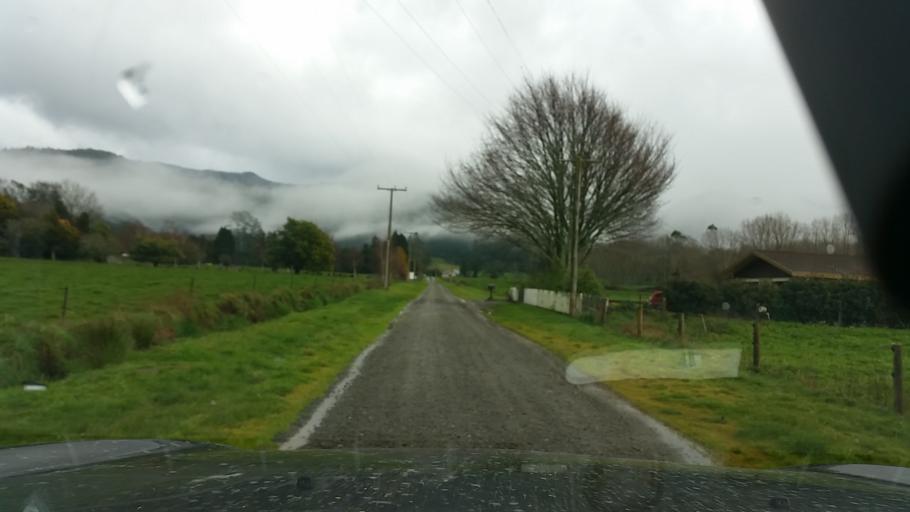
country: NZ
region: Nelson
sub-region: Nelson City
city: Nelson
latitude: -41.2390
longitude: 173.5794
